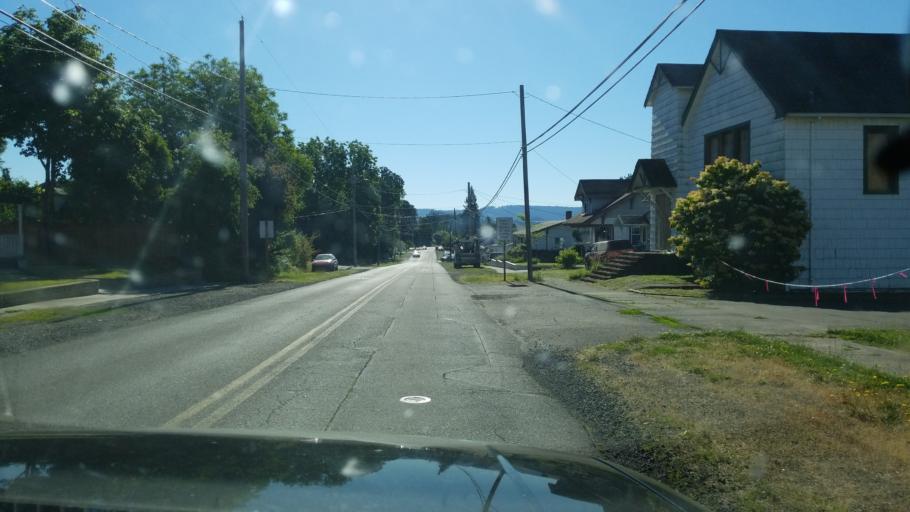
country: US
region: Oregon
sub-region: Yamhill County
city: Carlton
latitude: 45.2941
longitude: -123.1755
